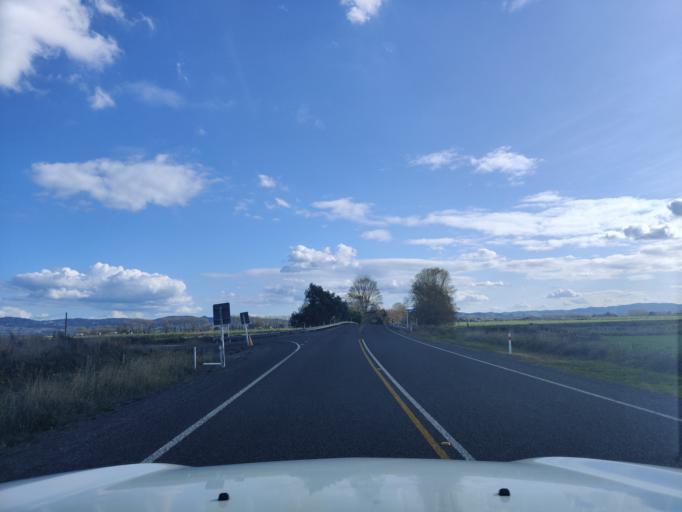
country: NZ
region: Waikato
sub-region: Hauraki District
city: Ngatea
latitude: -37.2786
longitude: 175.4565
